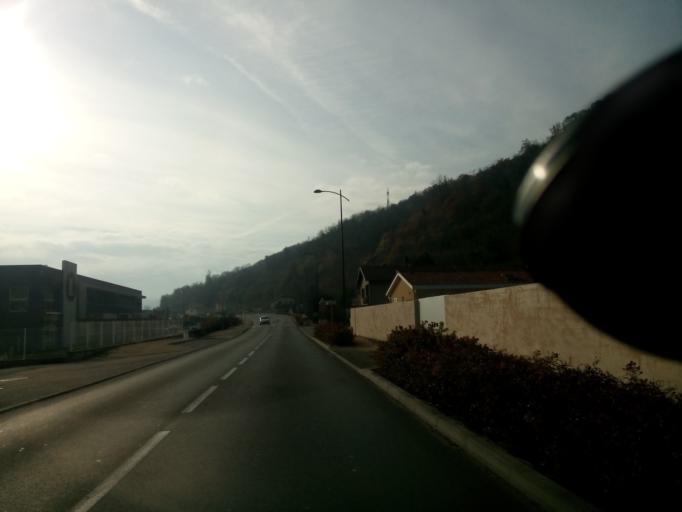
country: FR
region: Rhone-Alpes
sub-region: Departement de la Loire
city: Chavanay
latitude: 45.4305
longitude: 4.7417
